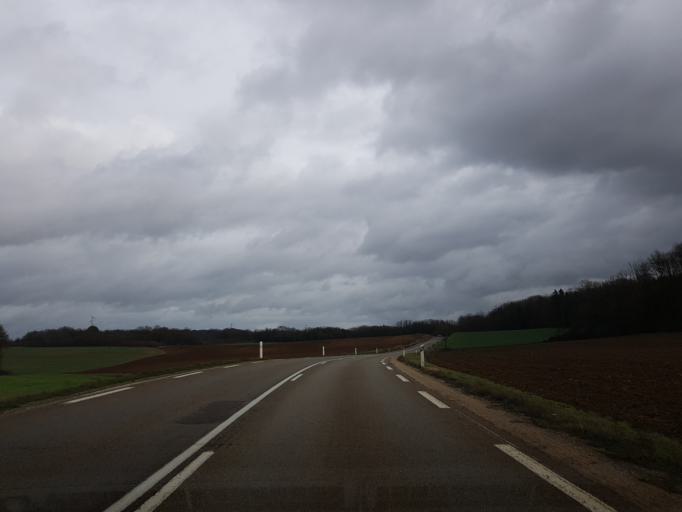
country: FR
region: Franche-Comte
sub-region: Departement de la Haute-Saone
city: Jussey
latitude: 47.7211
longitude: 5.8566
